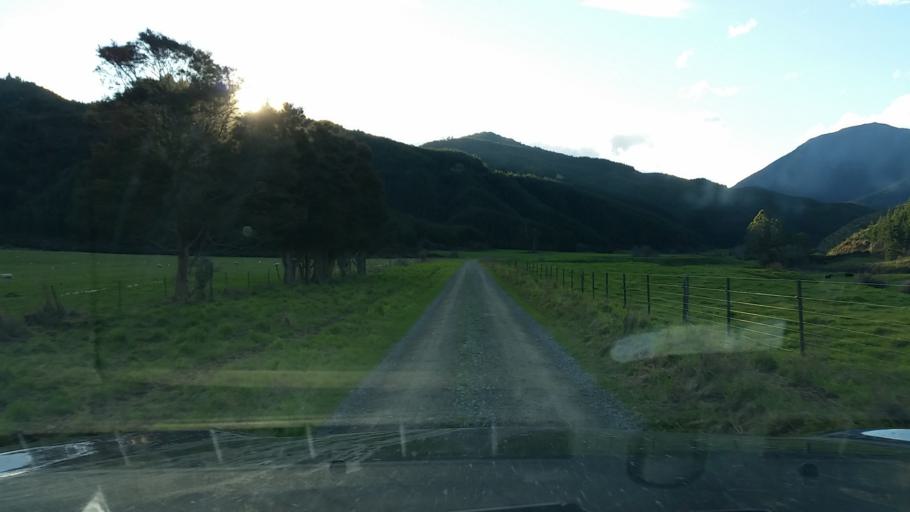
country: NZ
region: Nelson
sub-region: Nelson City
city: Nelson
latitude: -41.5371
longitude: 173.4910
